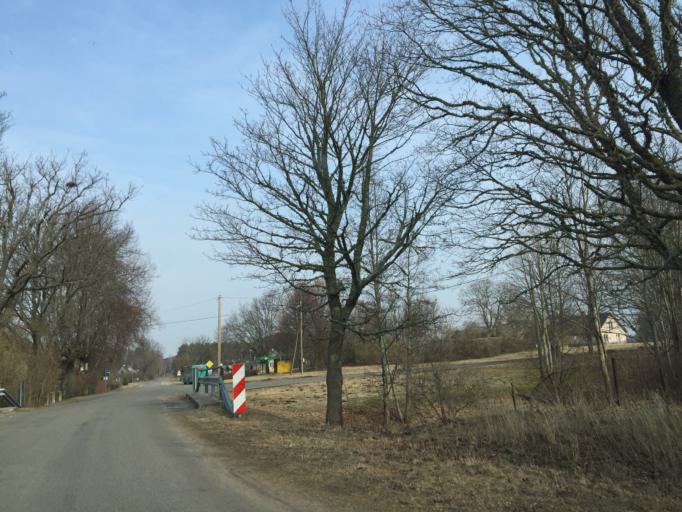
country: LV
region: Salacgrivas
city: Ainazi
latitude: 57.8763
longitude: 24.3620
